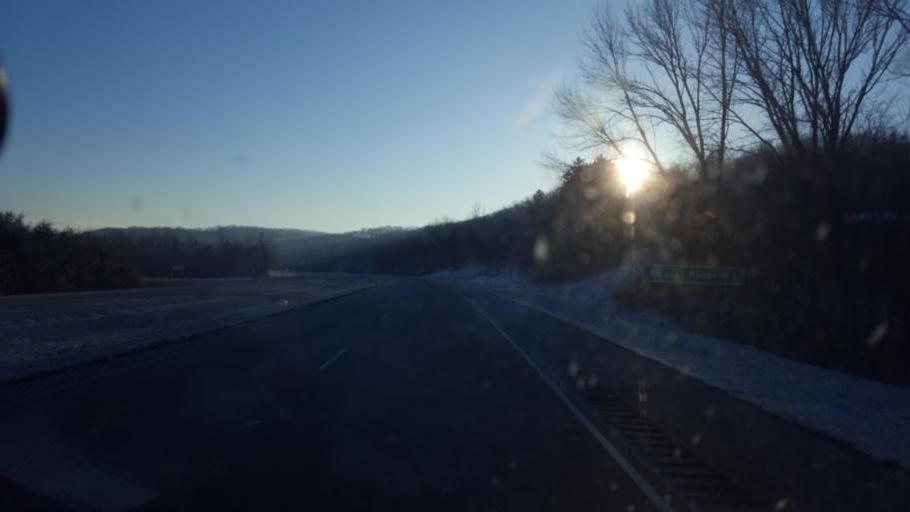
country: US
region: Ohio
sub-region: Pike County
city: Piketon
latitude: 39.0428
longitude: -83.1672
